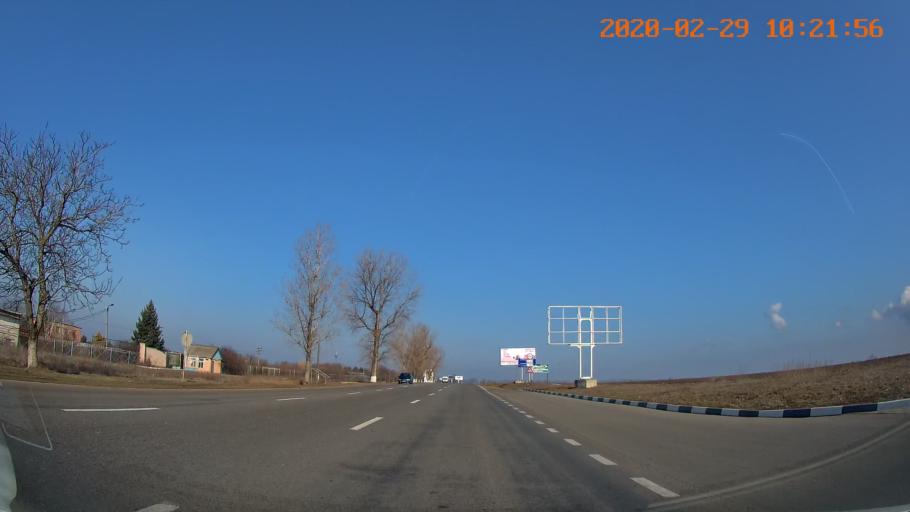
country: MD
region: Telenesti
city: Tiraspolul Nou
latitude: 46.8707
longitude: 29.6083
